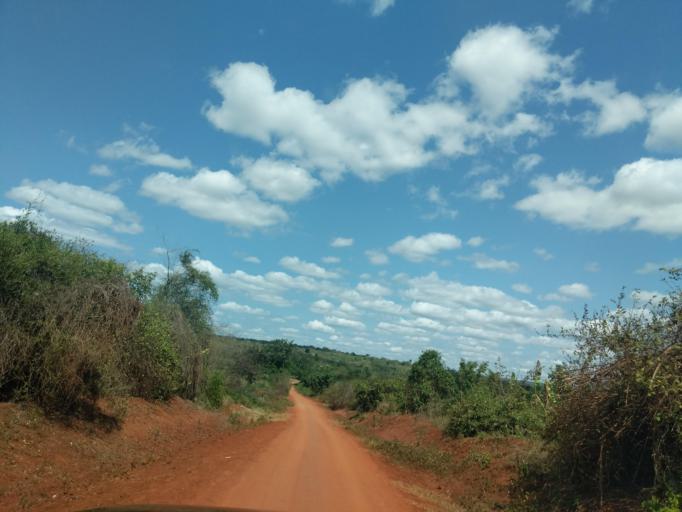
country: TZ
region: Tanga
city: Chanika
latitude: -5.5152
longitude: 38.3626
